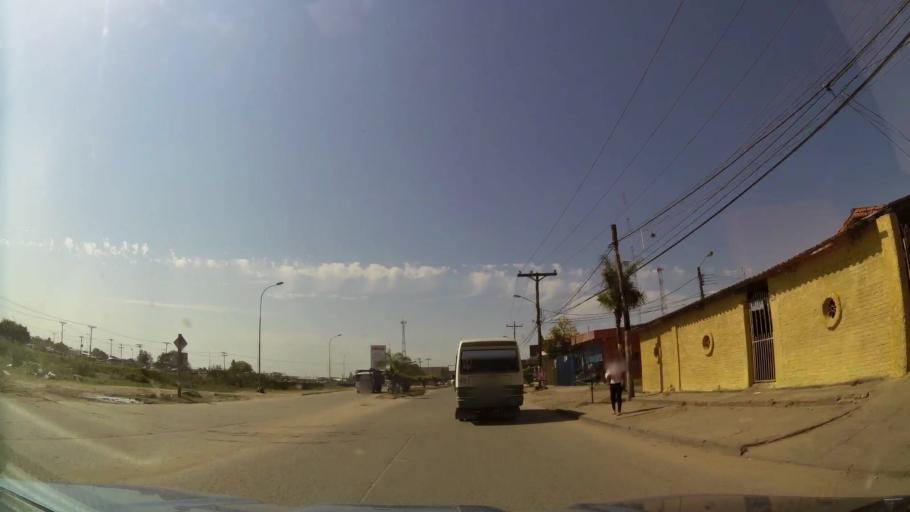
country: BO
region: Santa Cruz
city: Santa Cruz de la Sierra
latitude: -17.7529
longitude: -63.1299
